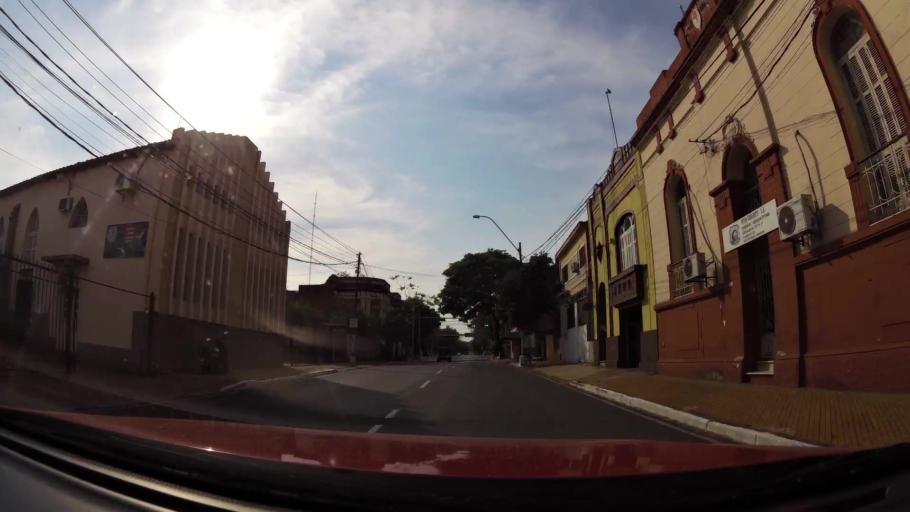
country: PY
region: Asuncion
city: Asuncion
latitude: -25.2867
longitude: -57.6241
